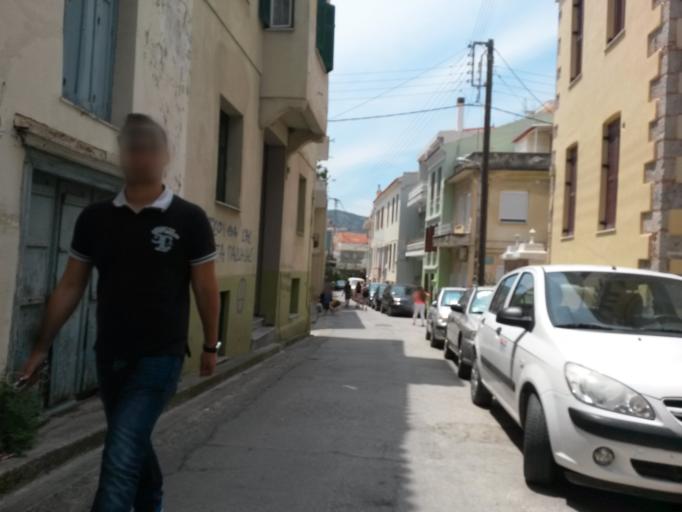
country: GR
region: North Aegean
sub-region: Nomos Lesvou
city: Mytilini
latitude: 39.1078
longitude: 26.5594
